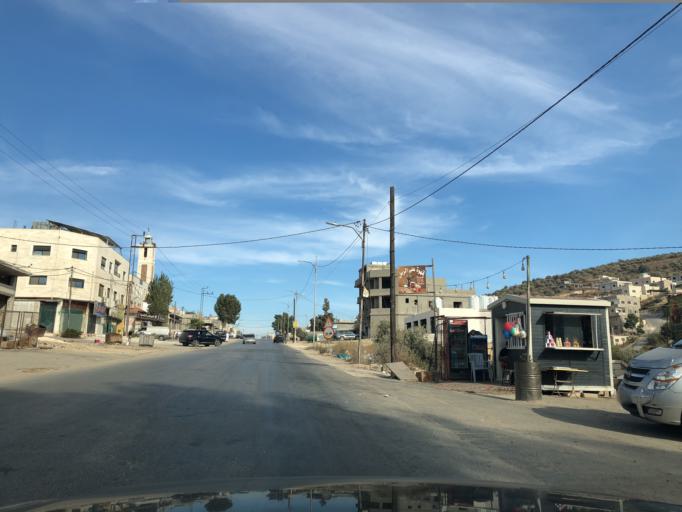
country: JO
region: Irbid
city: Sakib
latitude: 32.2791
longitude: 35.8013
